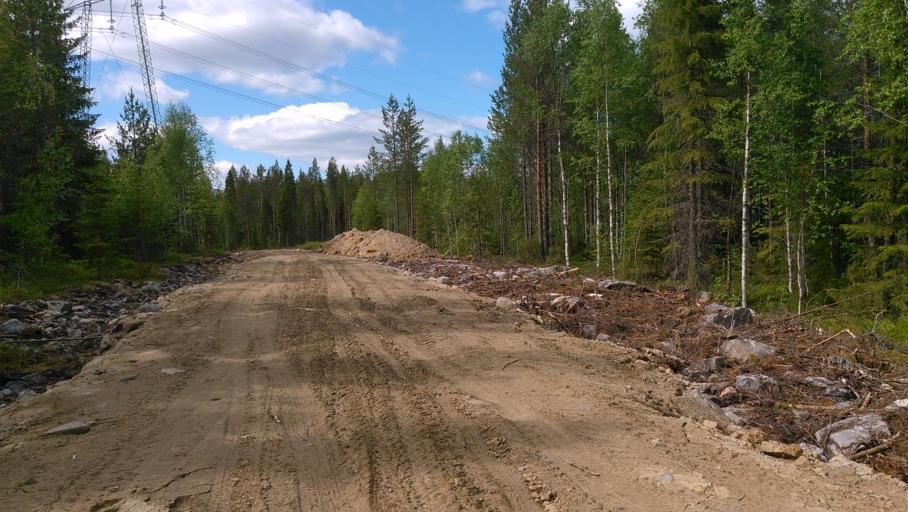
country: SE
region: Vaesterbotten
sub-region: Vannas Kommun
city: Vannasby
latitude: 63.9152
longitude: 19.9371
